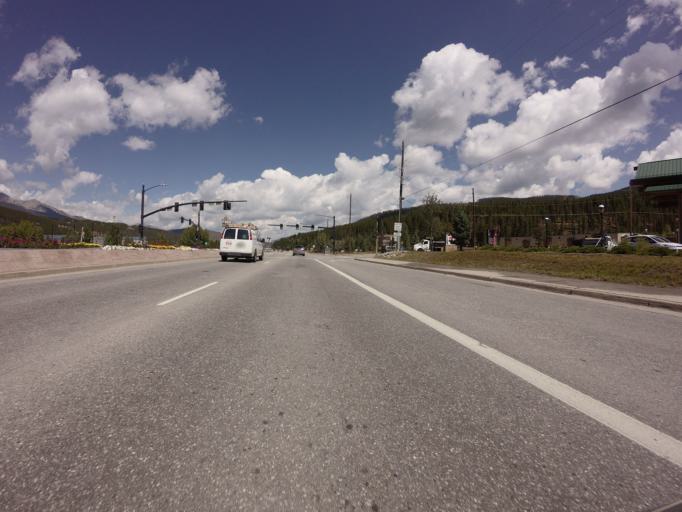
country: US
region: Colorado
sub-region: Summit County
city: Breckenridge
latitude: 39.4939
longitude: -106.0456
